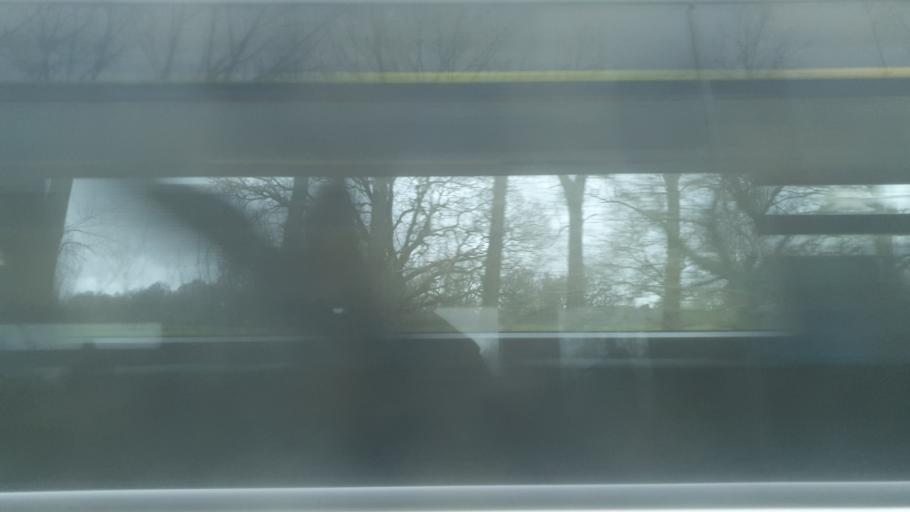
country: GB
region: England
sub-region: West Sussex
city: Pulborough
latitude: 50.9460
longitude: -0.5317
